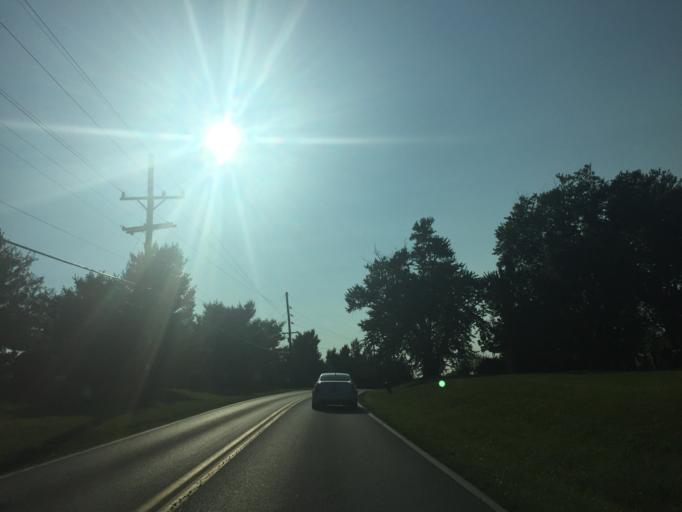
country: US
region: Maryland
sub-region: Carroll County
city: Mount Airy
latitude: 39.3445
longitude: -77.1966
